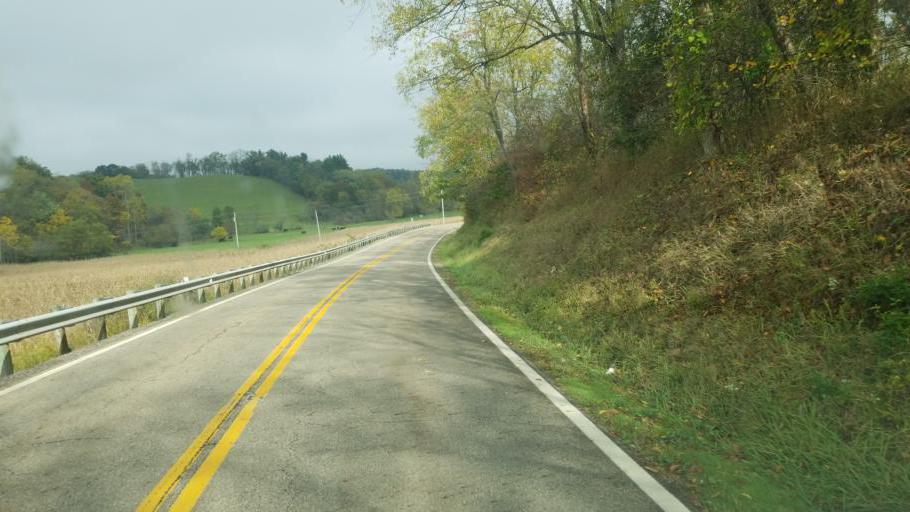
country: US
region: Ohio
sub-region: Carroll County
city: Lake Mohawk
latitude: 40.5745
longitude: -81.2565
